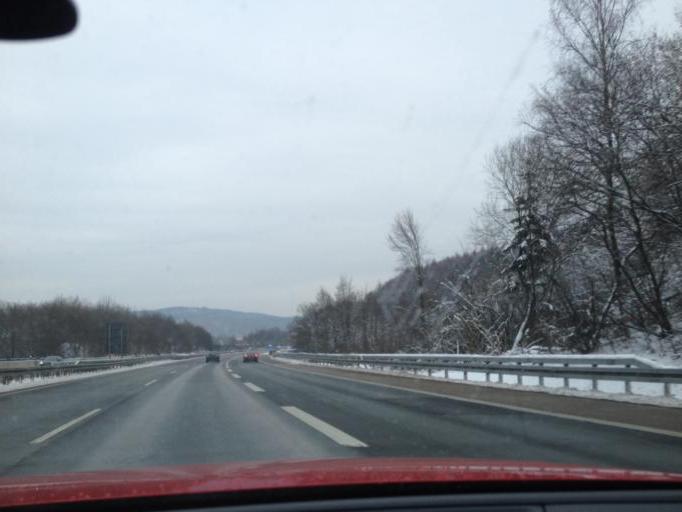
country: DE
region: North Rhine-Westphalia
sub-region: Regierungsbezirk Arnsberg
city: Siegen
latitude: 50.8616
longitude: 7.9827
